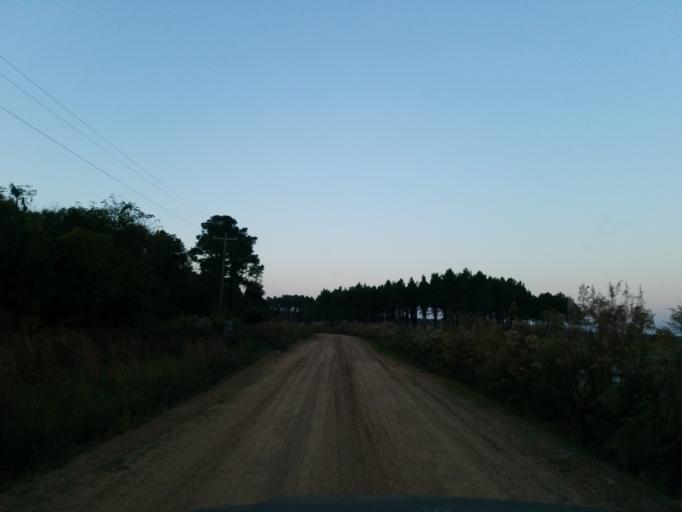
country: US
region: Georgia
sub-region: Turner County
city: Ashburn
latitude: 31.7258
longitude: -83.4817
